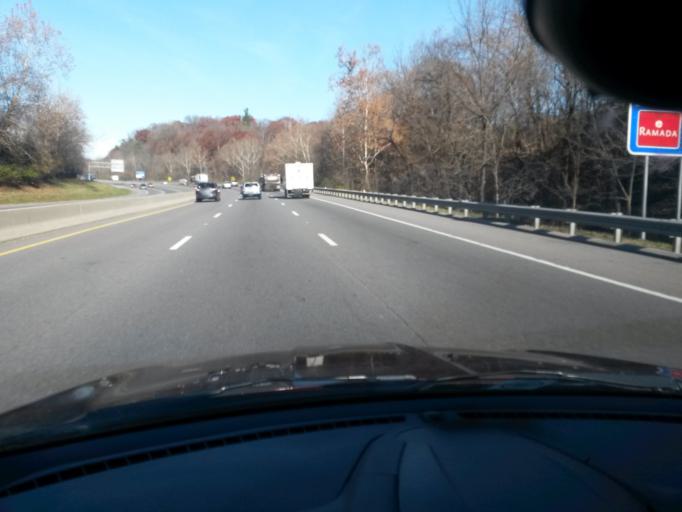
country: US
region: Virginia
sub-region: Roanoke County
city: Narrows
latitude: 37.2385
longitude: -79.9736
